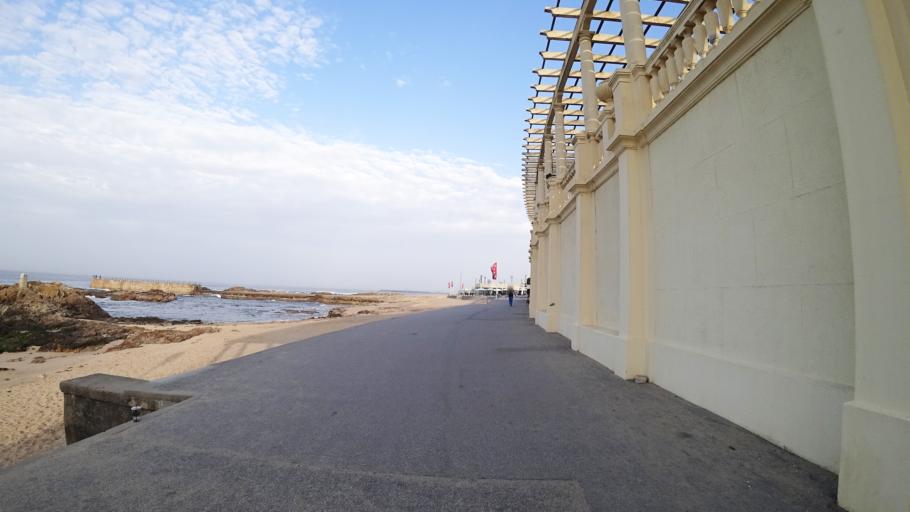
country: PT
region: Porto
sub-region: Matosinhos
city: Matosinhos
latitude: 41.1576
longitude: -8.6829
